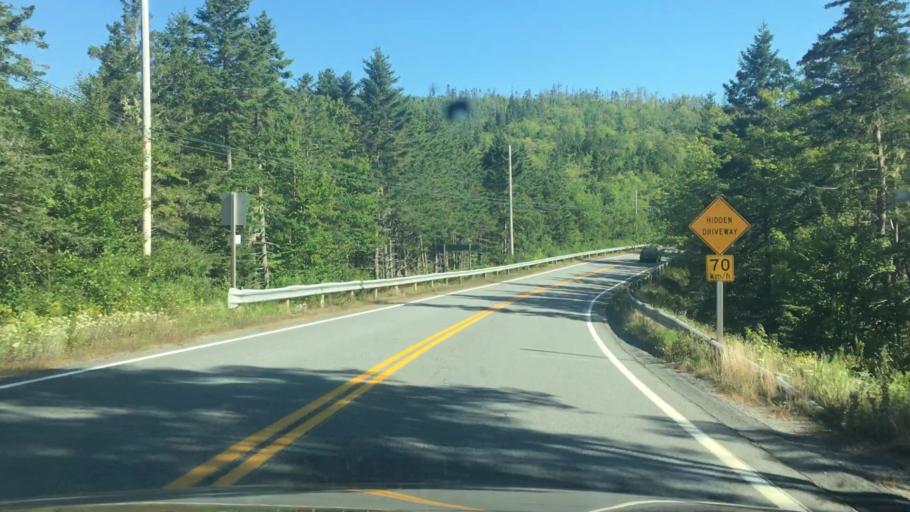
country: CA
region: Nova Scotia
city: Cole Harbour
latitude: 44.8152
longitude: -62.8852
